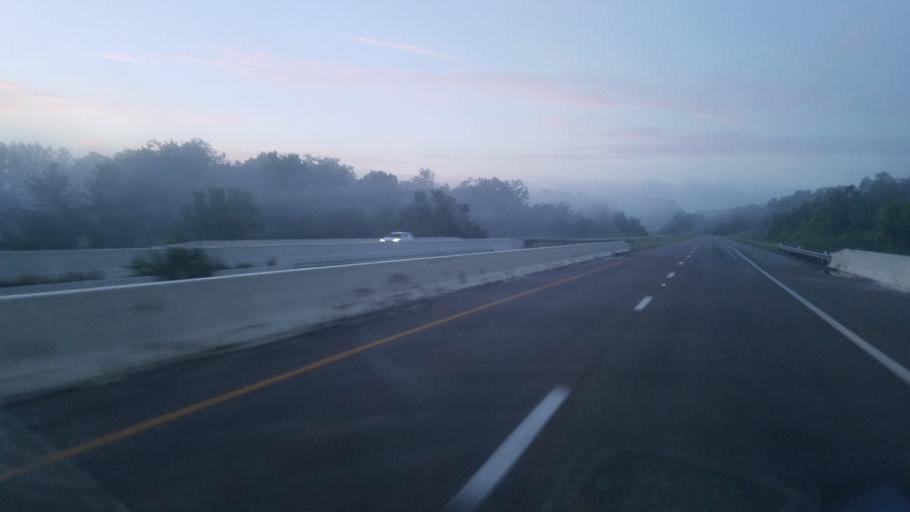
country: US
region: Ohio
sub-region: Ross County
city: Chillicothe
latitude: 39.2498
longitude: -82.8492
